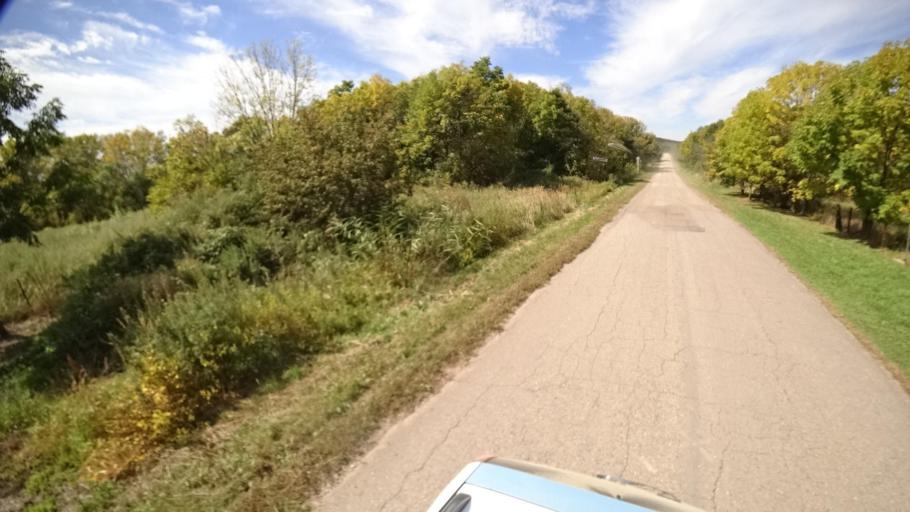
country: RU
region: Primorskiy
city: Yakovlevka
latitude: 44.6581
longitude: 133.7364
